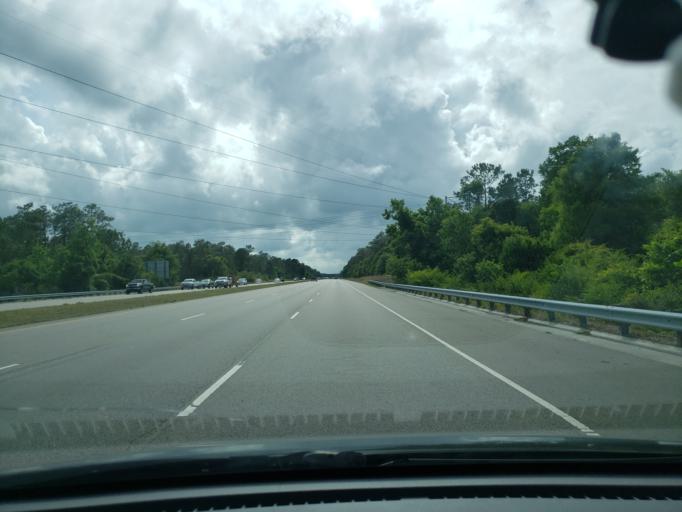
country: US
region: North Carolina
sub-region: New Hanover County
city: Kings Grant
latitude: 34.2549
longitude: -77.8795
